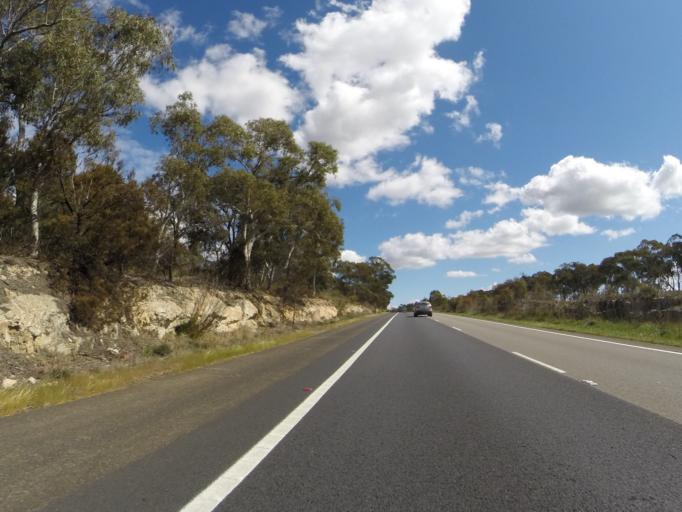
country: AU
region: New South Wales
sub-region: Goulburn Mulwaree
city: Goulburn
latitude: -34.7348
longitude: 149.9650
